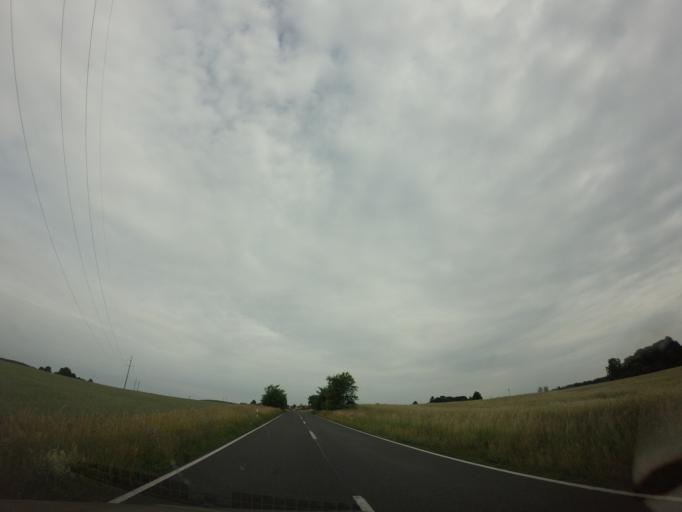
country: PL
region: West Pomeranian Voivodeship
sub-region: Powiat drawski
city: Wierzchowo
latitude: 53.4272
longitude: 16.2014
